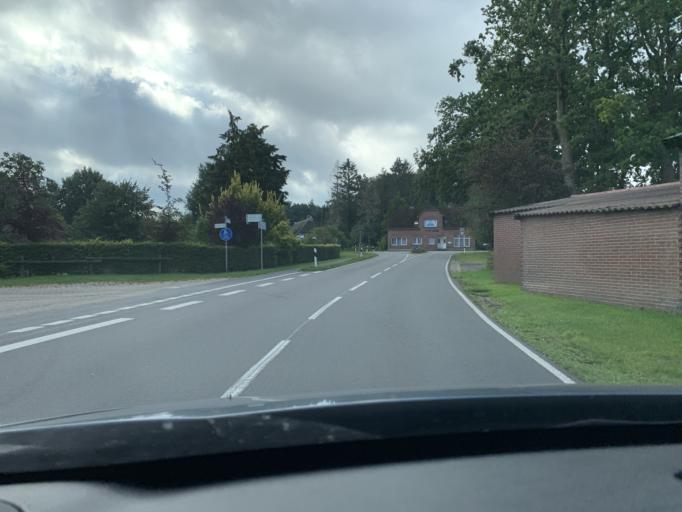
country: DE
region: Lower Saxony
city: Wardenburg
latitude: 53.0689
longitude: 8.1681
